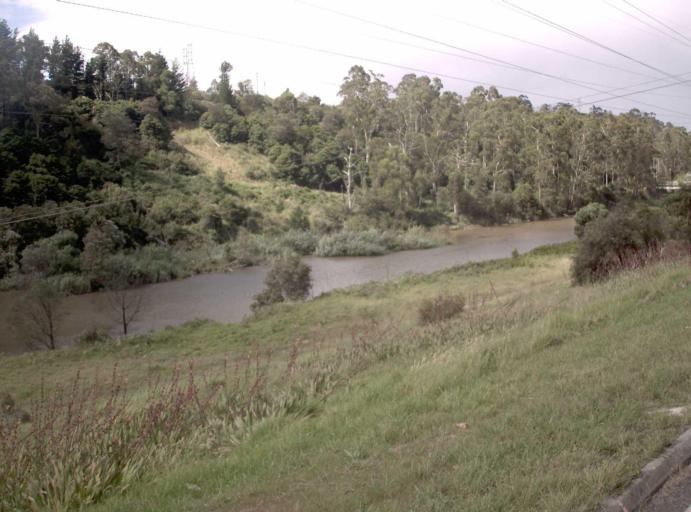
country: AU
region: Victoria
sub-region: Latrobe
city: Morwell
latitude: -38.1751
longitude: 146.3425
